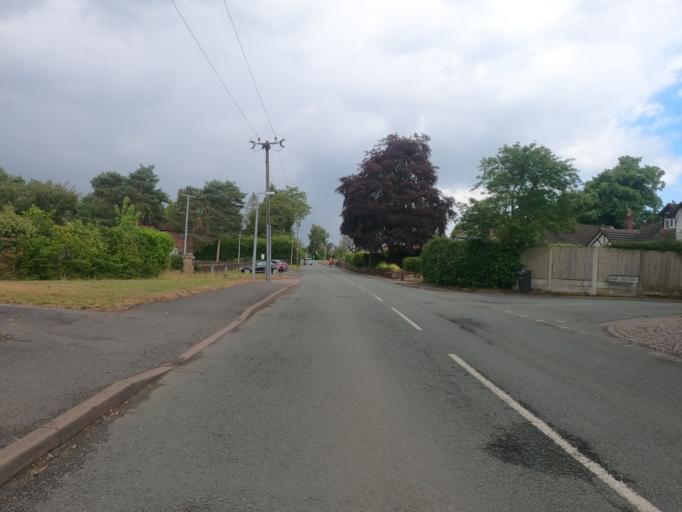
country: GB
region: England
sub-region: Cheshire West and Chester
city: Cuddington
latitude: 53.2407
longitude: -2.6052
